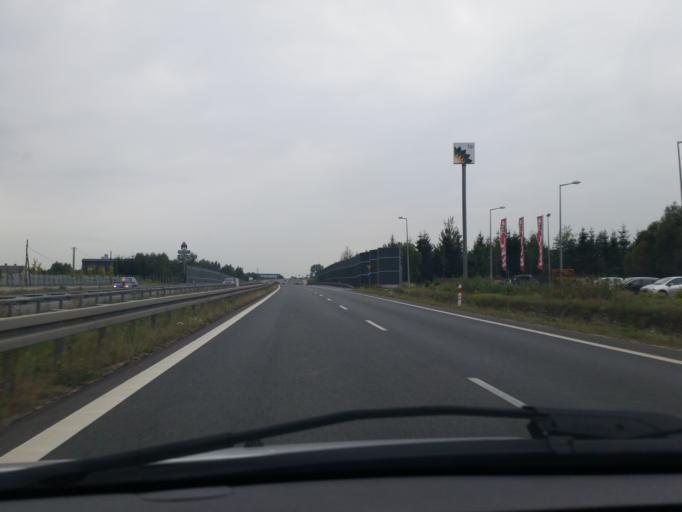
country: PL
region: Masovian Voivodeship
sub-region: Powiat zyrardowski
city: Radziejowice
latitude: 51.9937
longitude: 20.5468
